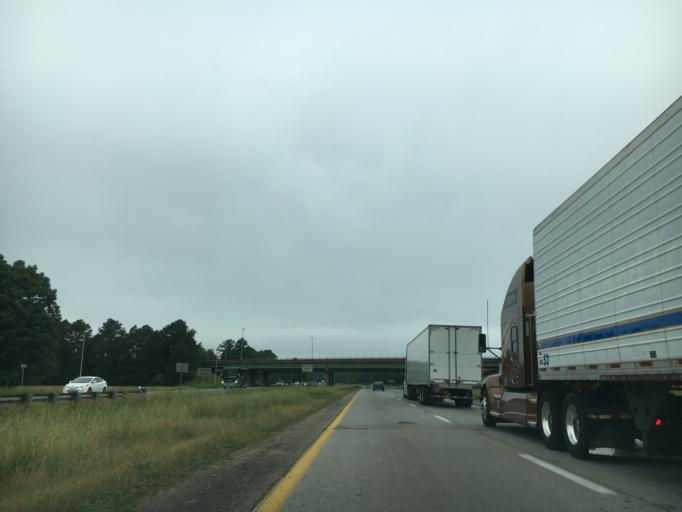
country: US
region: Virginia
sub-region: Chesterfield County
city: Matoaca
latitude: 37.1992
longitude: -77.4609
